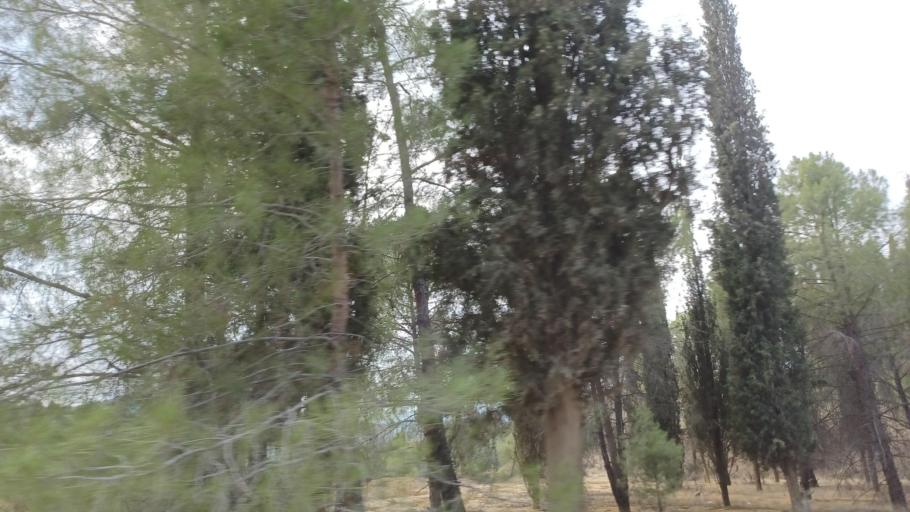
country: CY
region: Lefkosia
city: Klirou
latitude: 35.0412
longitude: 33.1093
